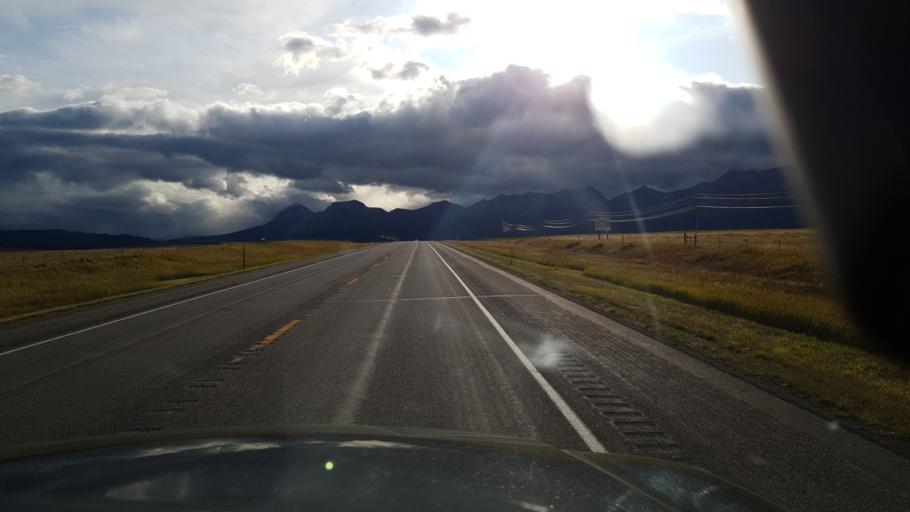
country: US
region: Montana
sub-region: Glacier County
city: South Browning
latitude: 48.4637
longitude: -113.1641
